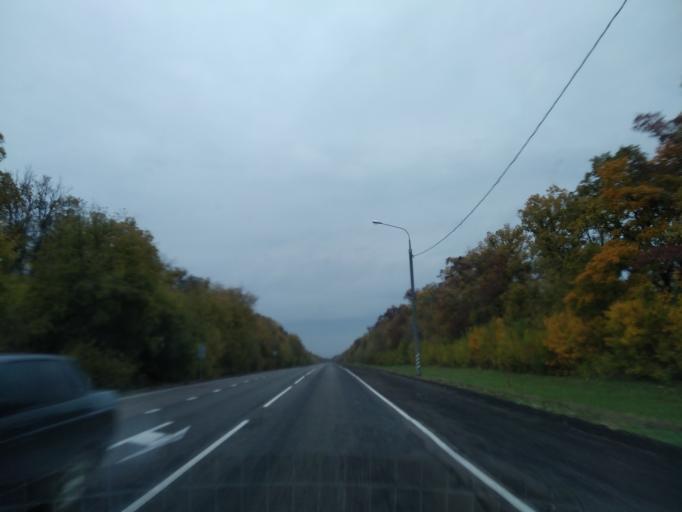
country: RU
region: Lipetsk
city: Zadonsk
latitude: 52.5055
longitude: 38.7576
